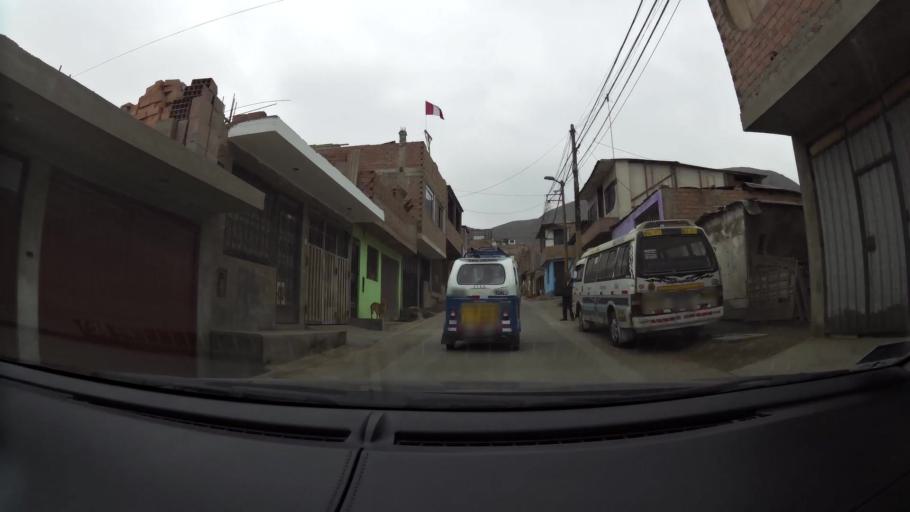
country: PE
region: Lima
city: Ventanilla
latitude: -11.9187
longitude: -77.0906
